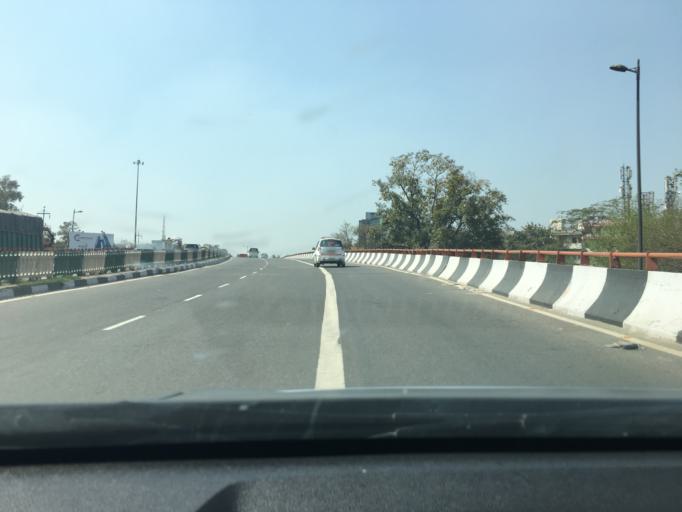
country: IN
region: NCT
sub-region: North Delhi
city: Delhi
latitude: 28.6614
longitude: 77.2406
